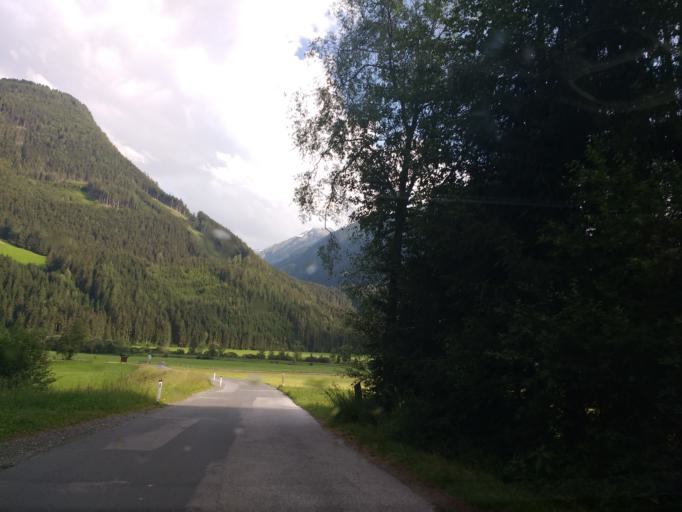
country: AT
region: Salzburg
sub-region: Politischer Bezirk Zell am See
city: Neukirchen am Grossvenediger
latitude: 47.2454
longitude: 12.2620
